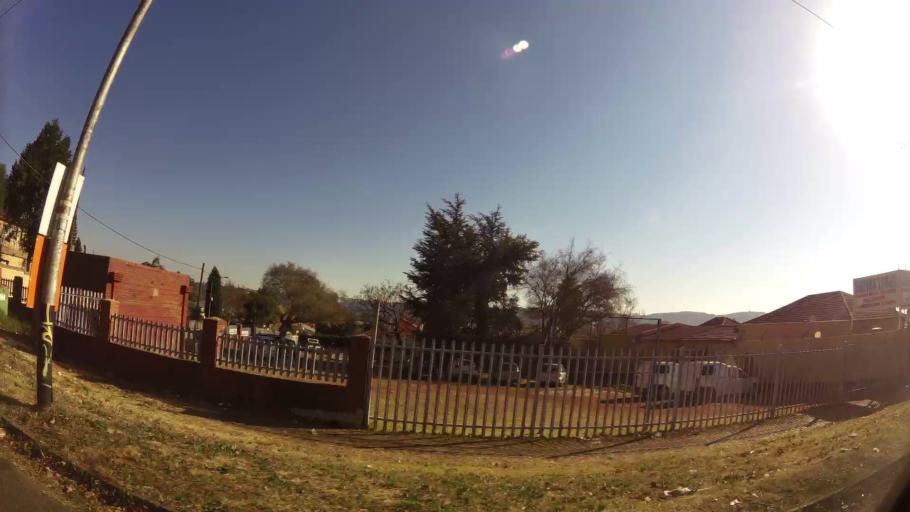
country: ZA
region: Gauteng
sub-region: City of Johannesburg Metropolitan Municipality
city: Johannesburg
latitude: -26.1920
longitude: 28.1023
